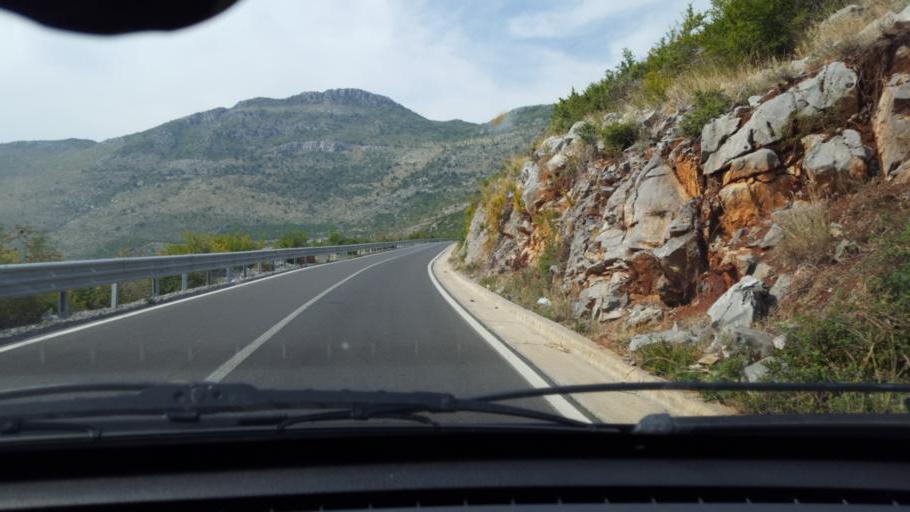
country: AL
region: Shkoder
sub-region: Rrethi i Malesia e Madhe
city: Hot
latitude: 42.3738
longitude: 19.4543
